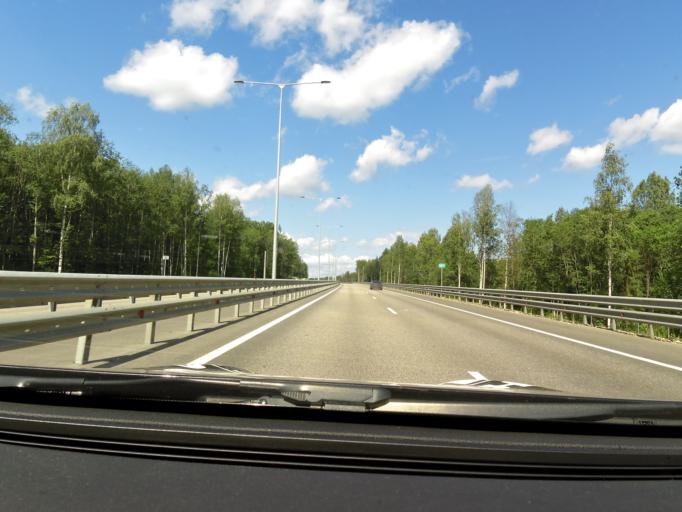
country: RU
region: Tverskaya
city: Vydropuzhsk
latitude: 57.3548
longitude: 34.6955
